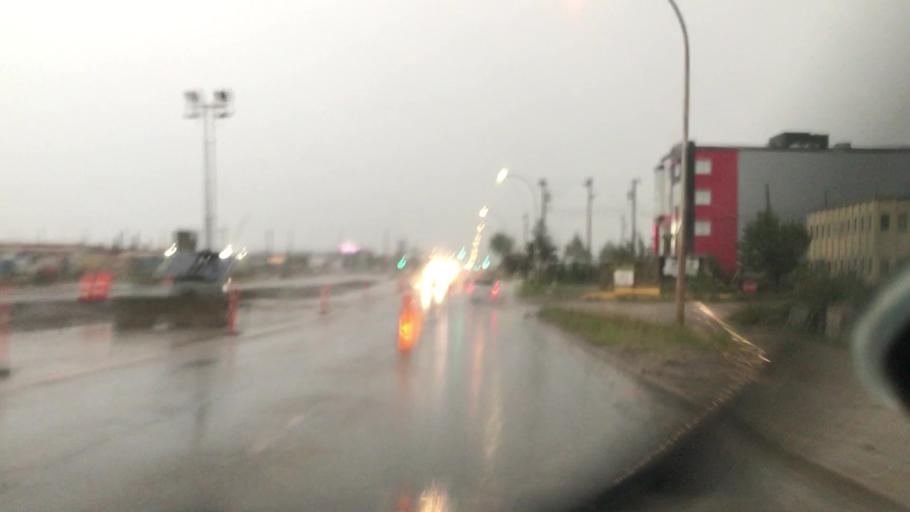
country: CA
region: Alberta
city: Edmonton
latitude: 53.4992
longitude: -113.4426
